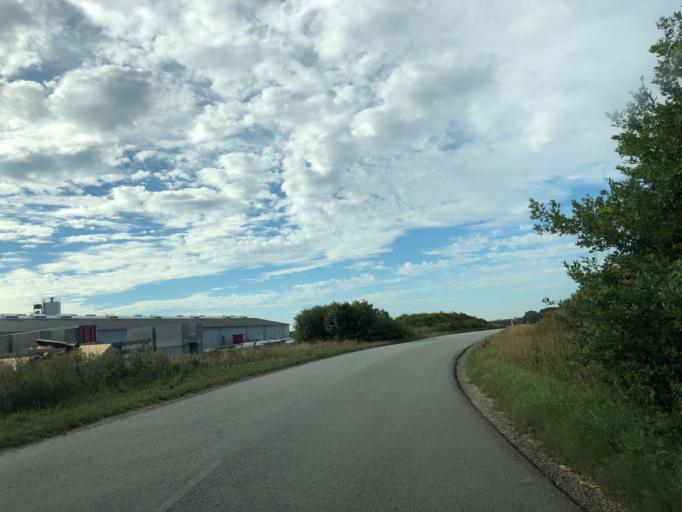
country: DK
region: Central Jutland
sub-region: Holstebro Kommune
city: Ulfborg
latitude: 56.1212
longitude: 8.4215
